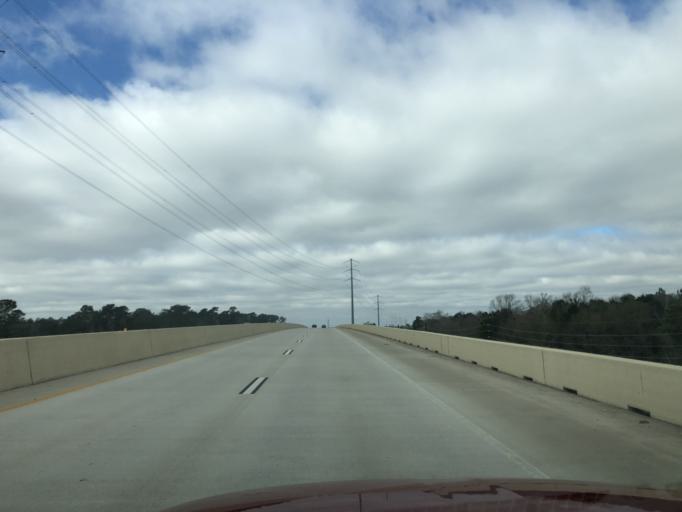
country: US
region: Texas
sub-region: Montgomery County
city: The Woodlands
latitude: 30.0944
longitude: -95.4913
